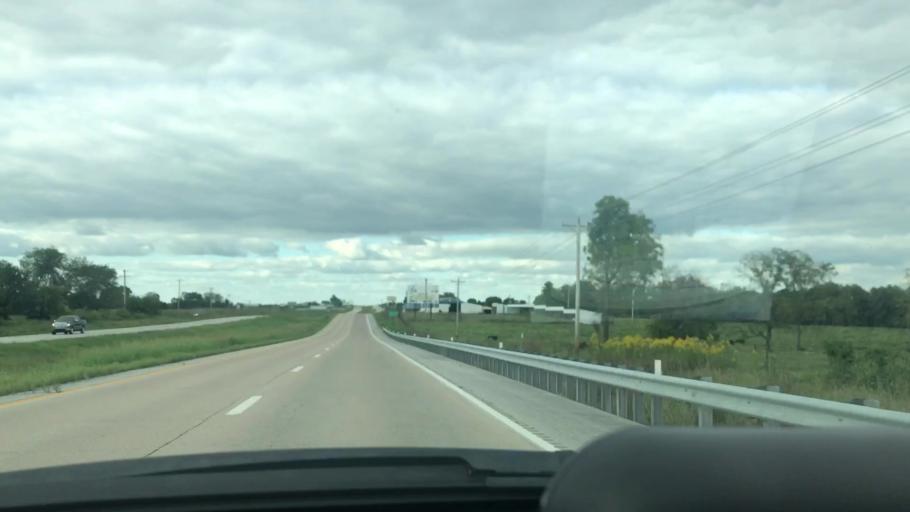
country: US
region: Missouri
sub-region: Benton County
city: Lincoln
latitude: 38.3288
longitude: -93.3415
